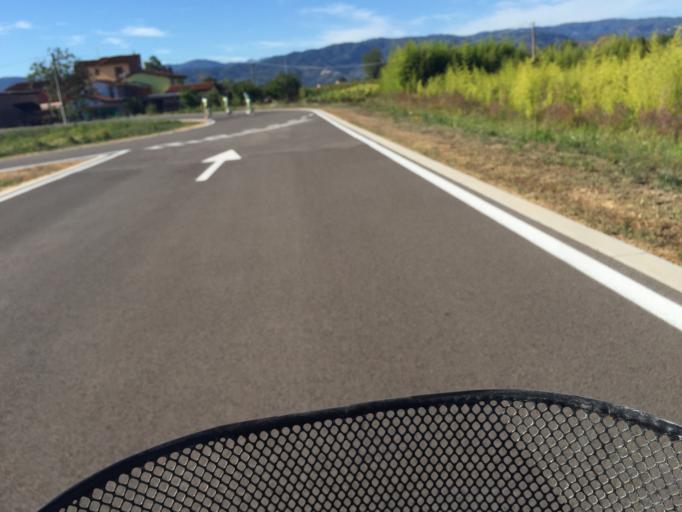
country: IT
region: Tuscany
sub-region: Provincia di Pistoia
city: Anchione
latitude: 43.8414
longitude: 10.7654
